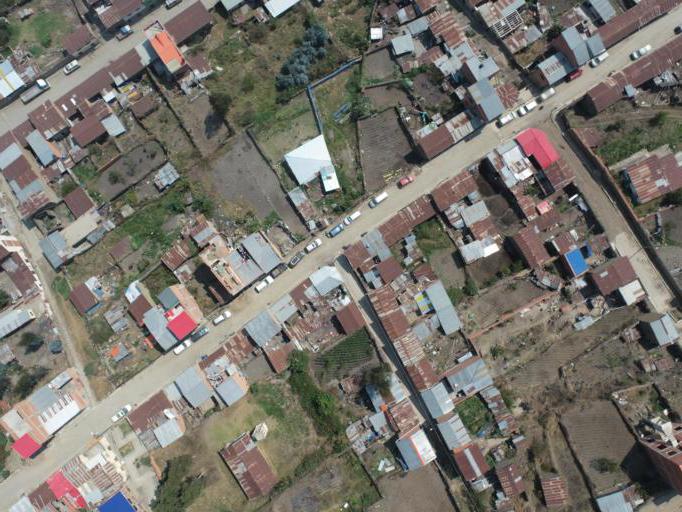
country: BO
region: La Paz
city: Quime
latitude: -16.9822
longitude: -67.2174
